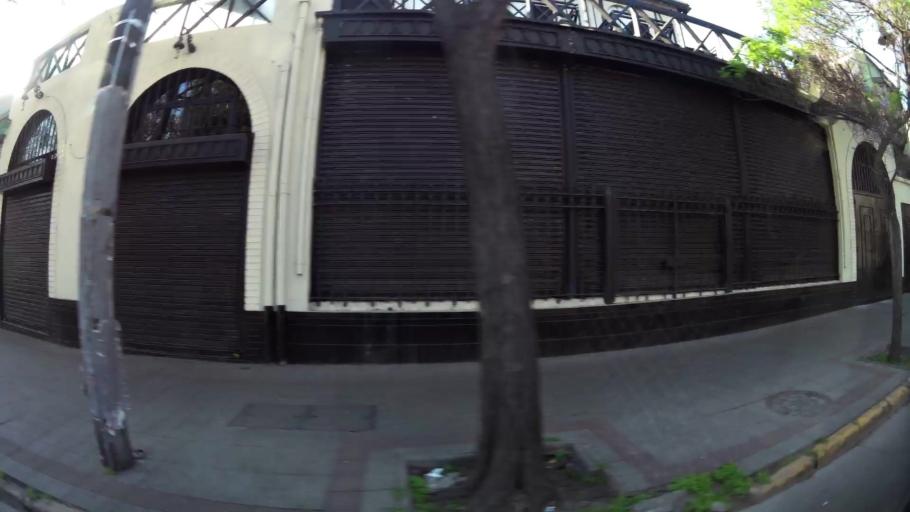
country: CL
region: Santiago Metropolitan
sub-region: Provincia de Santiago
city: Santiago
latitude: -33.4318
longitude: -70.6338
